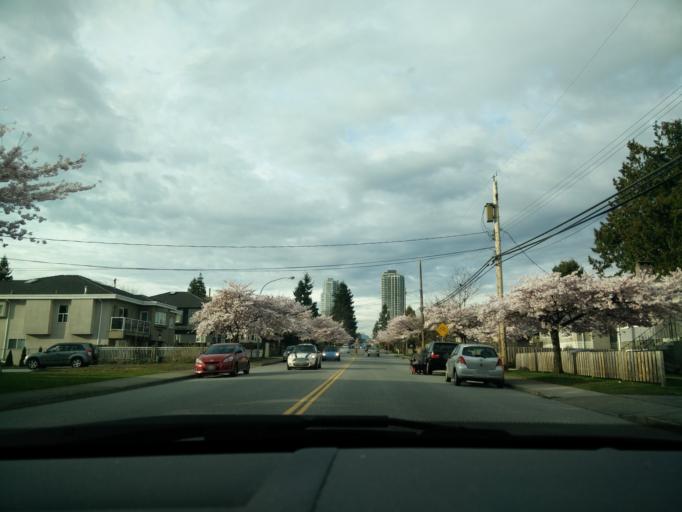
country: CA
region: British Columbia
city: Burnaby
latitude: 49.2175
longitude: -122.9940
